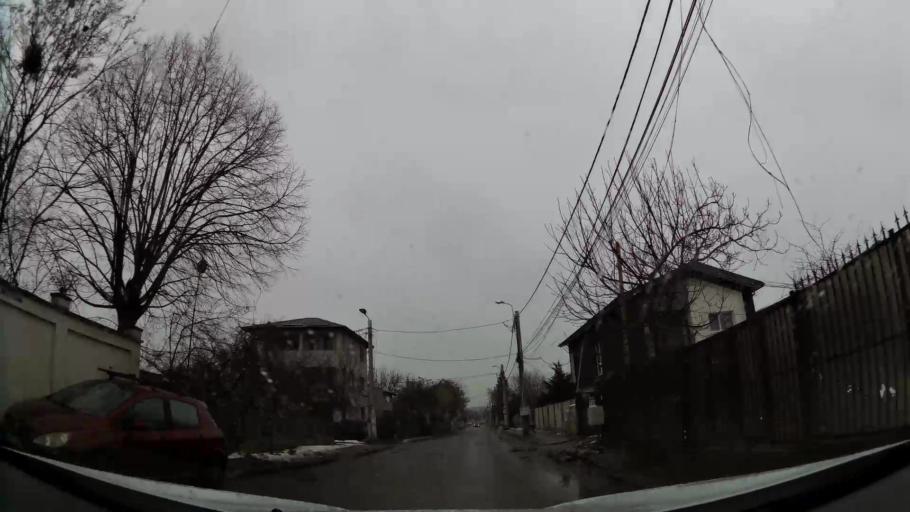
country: RO
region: Ilfov
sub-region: Comuna Chiajna
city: Rosu
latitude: 44.4060
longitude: 26.0160
